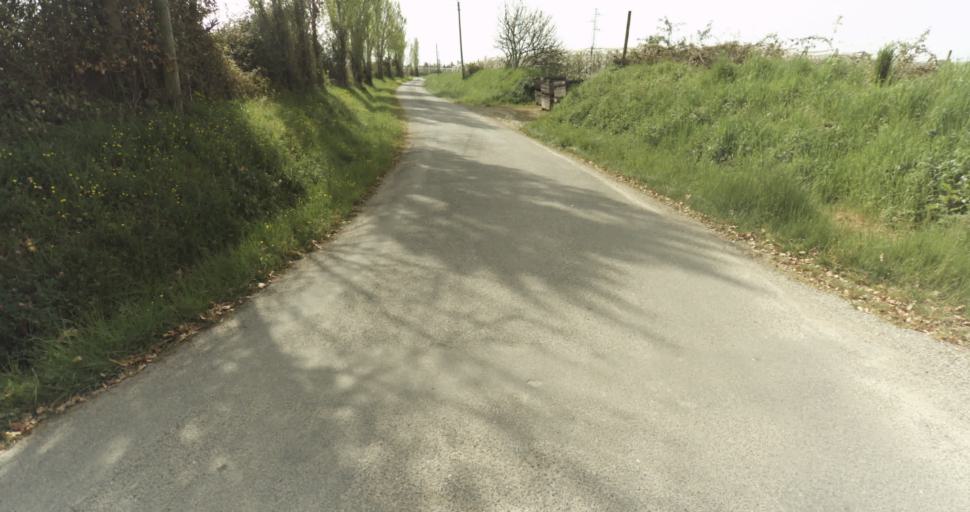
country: FR
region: Midi-Pyrenees
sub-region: Departement du Tarn-et-Garonne
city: Moissac
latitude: 44.0953
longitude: 1.0693
